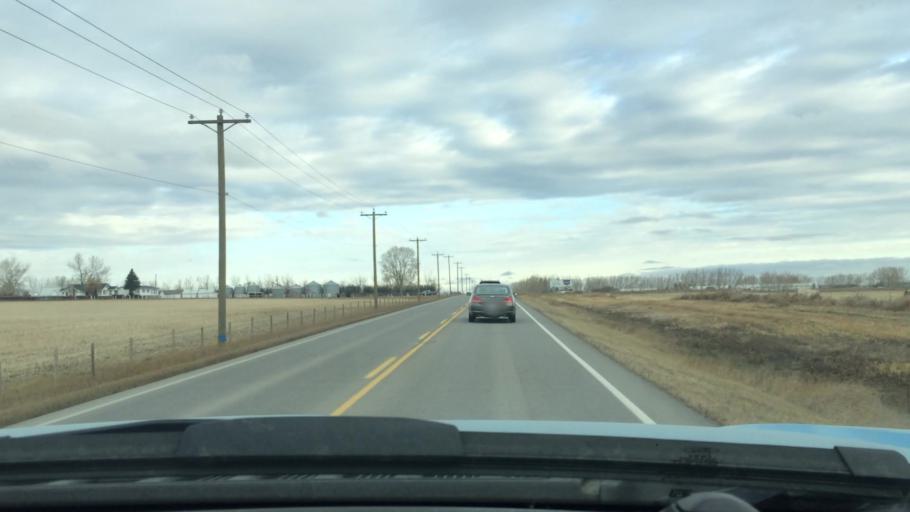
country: CA
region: Alberta
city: Airdrie
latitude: 51.2250
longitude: -114.0249
